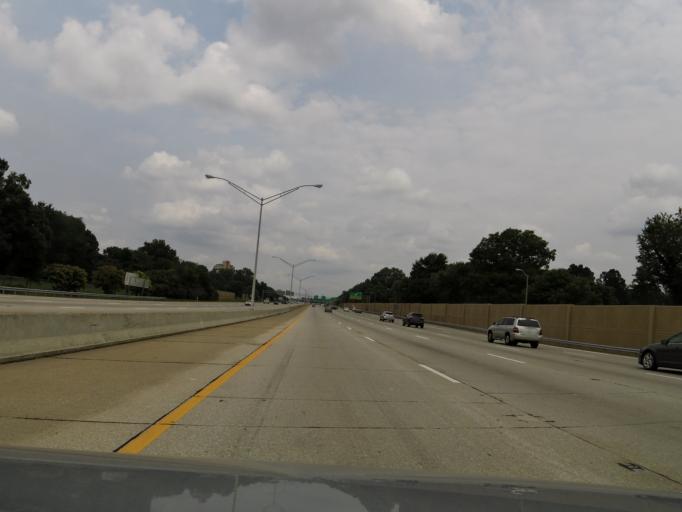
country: US
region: Kentucky
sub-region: Jefferson County
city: Buechel
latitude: 38.2232
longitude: -85.6471
